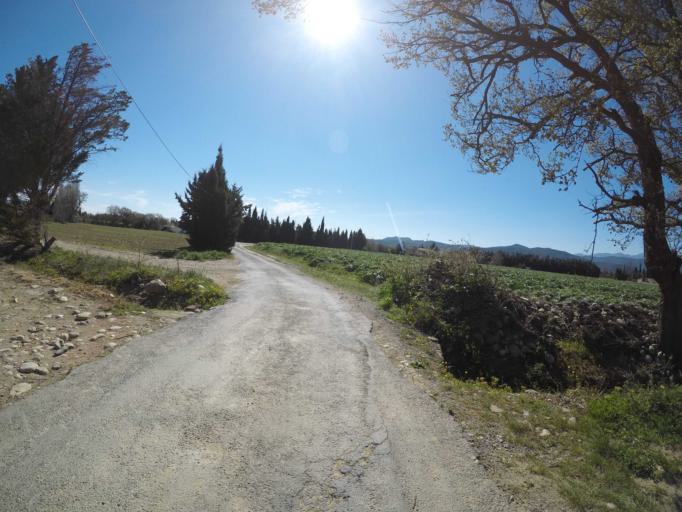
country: FR
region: Languedoc-Roussillon
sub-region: Departement des Pyrenees-Orientales
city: Ille-sur-Tet
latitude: 42.6881
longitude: 2.6544
